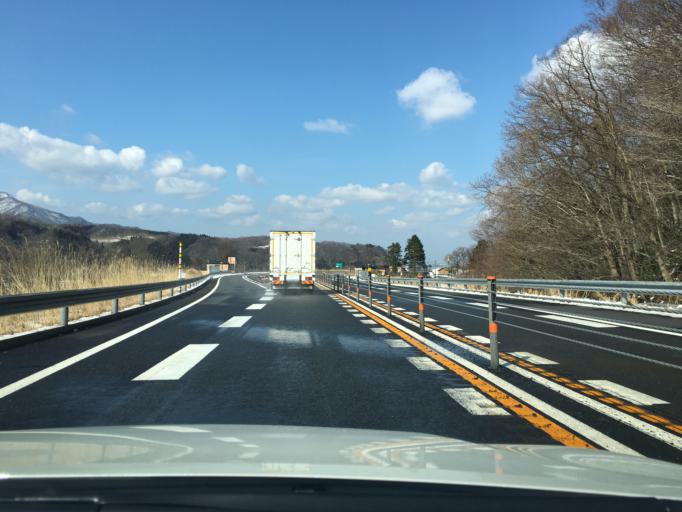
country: JP
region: Yamagata
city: Tsuruoka
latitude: 38.6091
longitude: 139.8425
